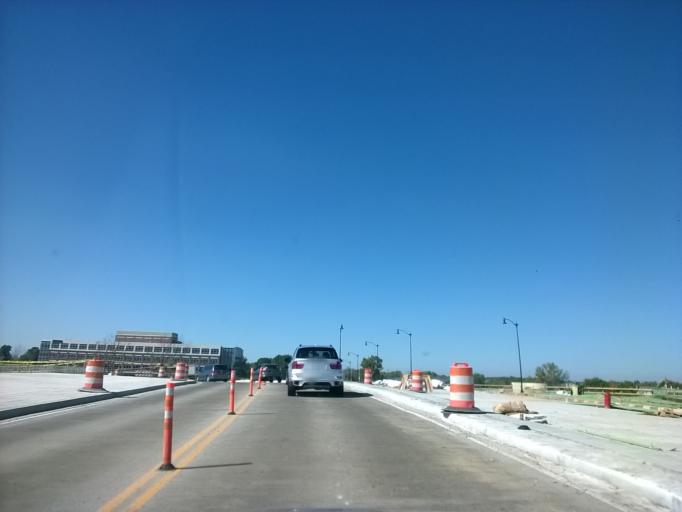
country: US
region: Indiana
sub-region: Hamilton County
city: Carmel
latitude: 39.9779
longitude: -86.1572
